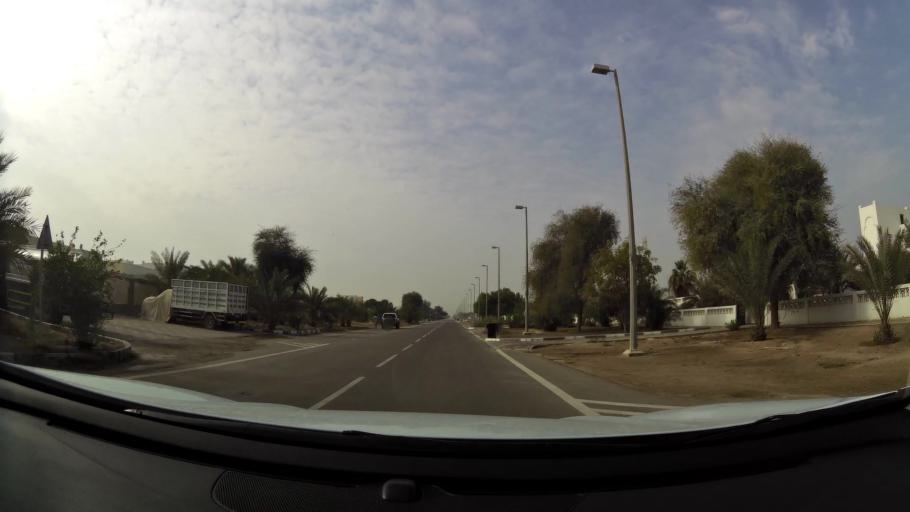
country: AE
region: Abu Dhabi
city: Abu Dhabi
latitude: 24.6676
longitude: 54.7666
